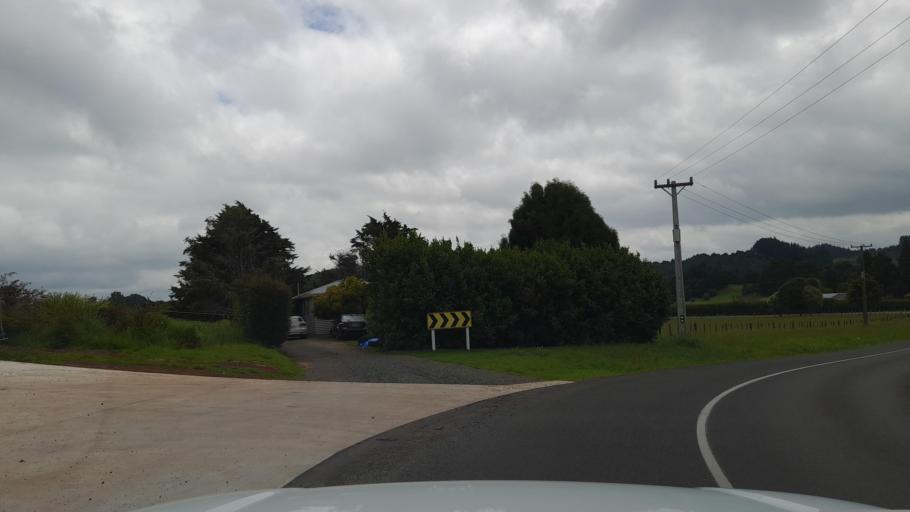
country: NZ
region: Northland
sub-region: Far North District
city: Waimate North
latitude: -35.4062
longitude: 173.7851
